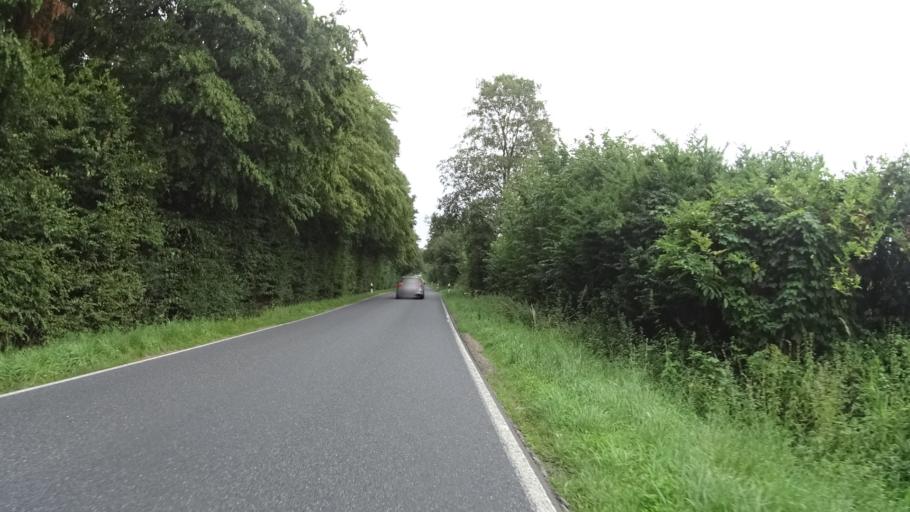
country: DE
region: Schleswig-Holstein
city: Kuhsen
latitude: 53.6845
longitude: 10.6002
